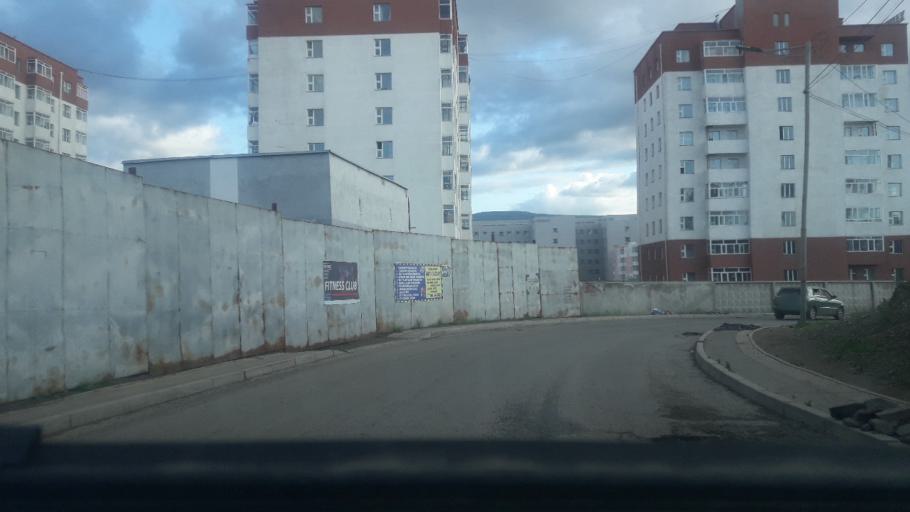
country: MN
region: Ulaanbaatar
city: Ulaanbaatar
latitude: 47.9179
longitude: 106.9955
